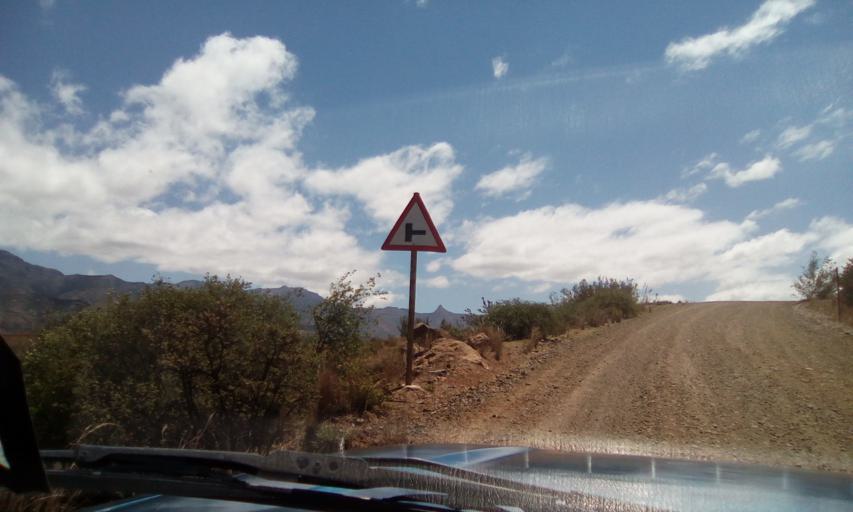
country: LS
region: Qacha's Nek
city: Qacha's Nek
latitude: -30.0638
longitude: 28.6232
